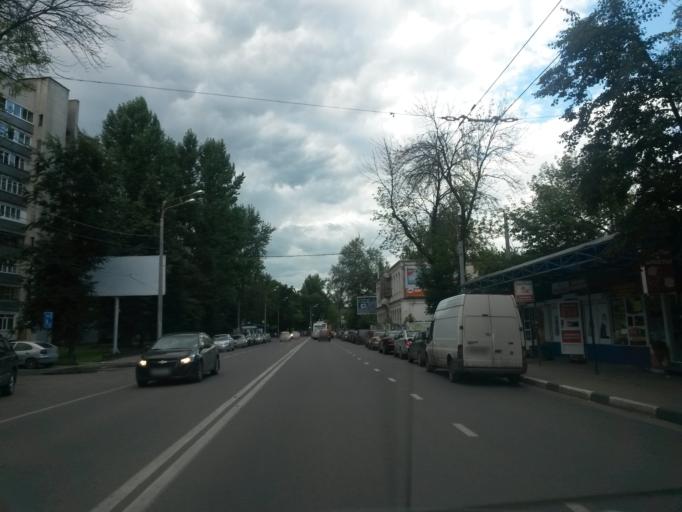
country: RU
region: Jaroslavl
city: Yaroslavl
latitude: 57.6358
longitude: 39.8813
